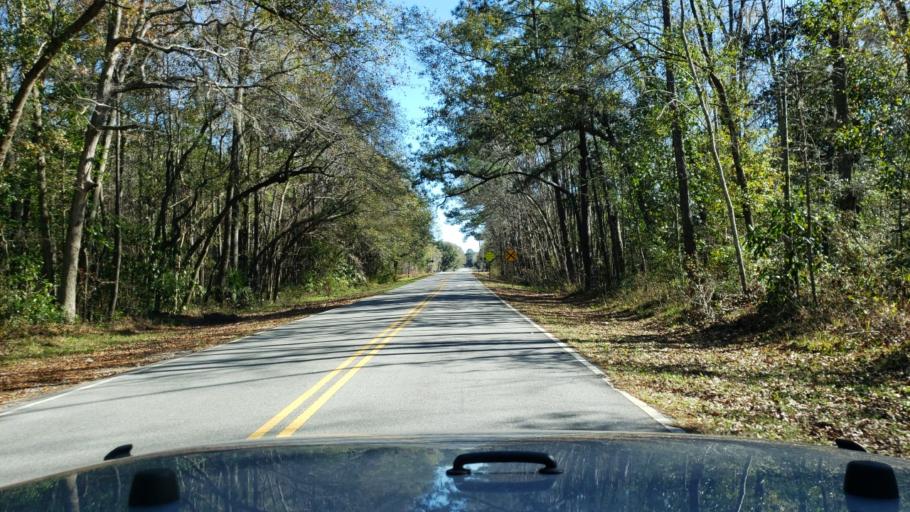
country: US
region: Georgia
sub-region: Chatham County
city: Georgetown
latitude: 32.0319
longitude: -81.1836
